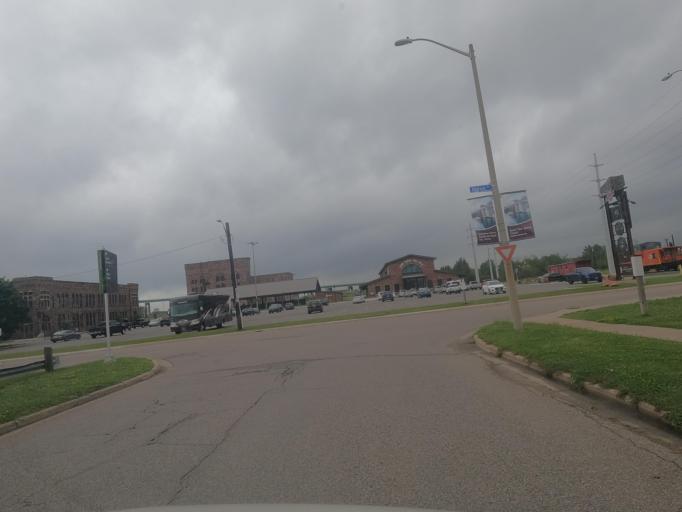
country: CA
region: Ontario
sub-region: Algoma
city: Sault Ste. Marie
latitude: 46.5164
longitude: -84.3479
